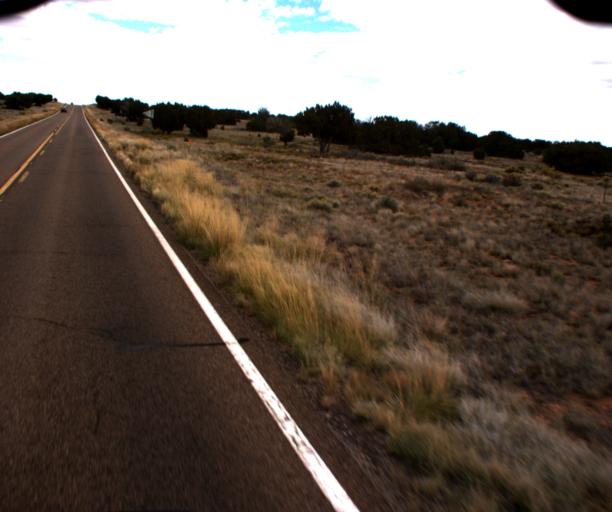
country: US
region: Arizona
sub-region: Navajo County
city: Heber-Overgaard
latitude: 34.5073
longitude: -110.4483
